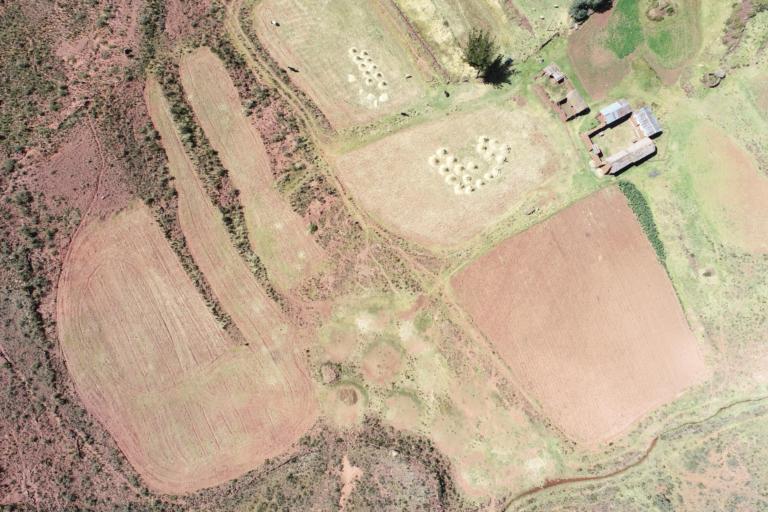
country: BO
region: La Paz
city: Tiahuanaco
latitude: -16.6067
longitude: -68.7710
